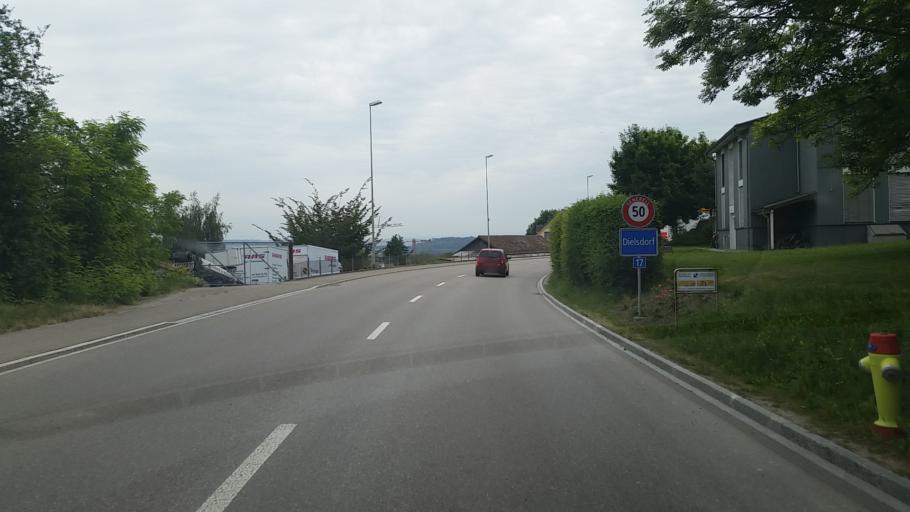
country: CH
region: Zurich
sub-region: Bezirk Dielsdorf
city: Dielsdorf
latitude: 47.4864
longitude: 8.4513
